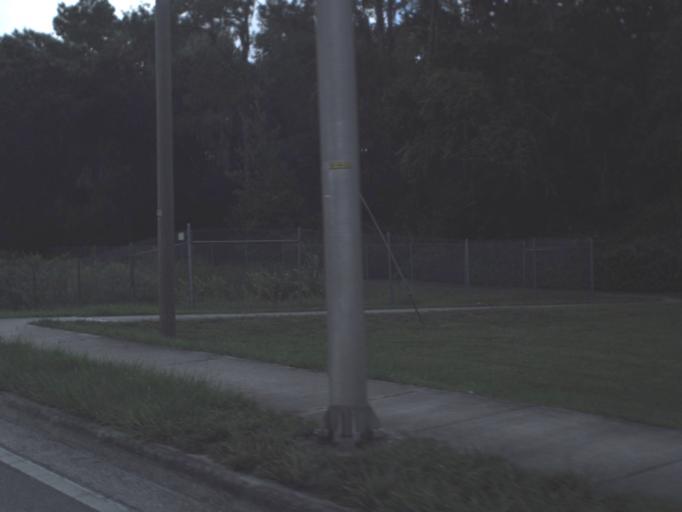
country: US
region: Florida
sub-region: Hillsborough County
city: Plant City
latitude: 28.0316
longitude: -82.1049
